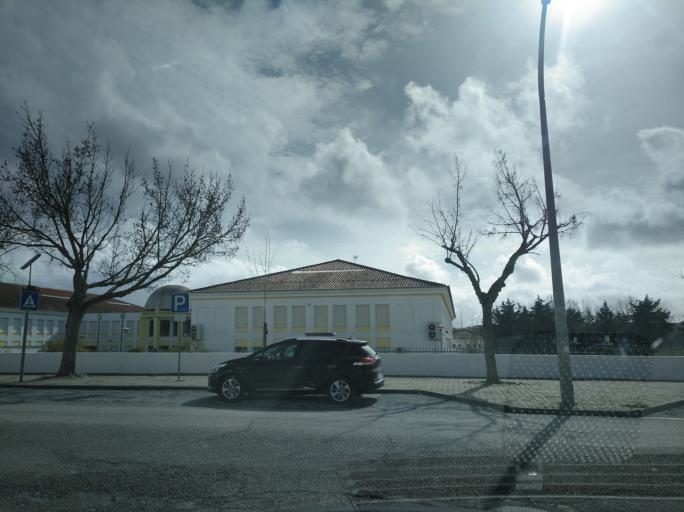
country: PT
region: Setubal
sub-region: Grandola
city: Grandola
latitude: 38.1739
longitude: -8.5613
